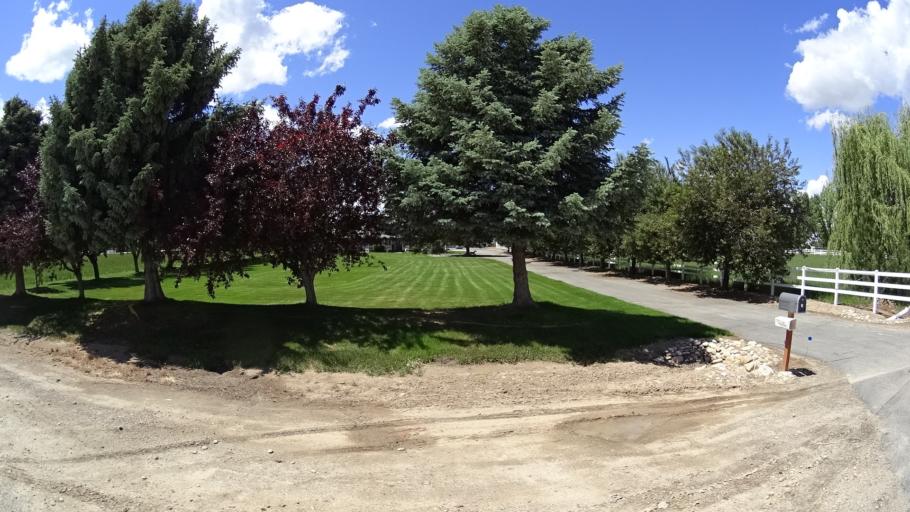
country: US
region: Idaho
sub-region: Ada County
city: Meridian
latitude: 43.5786
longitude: -116.4537
